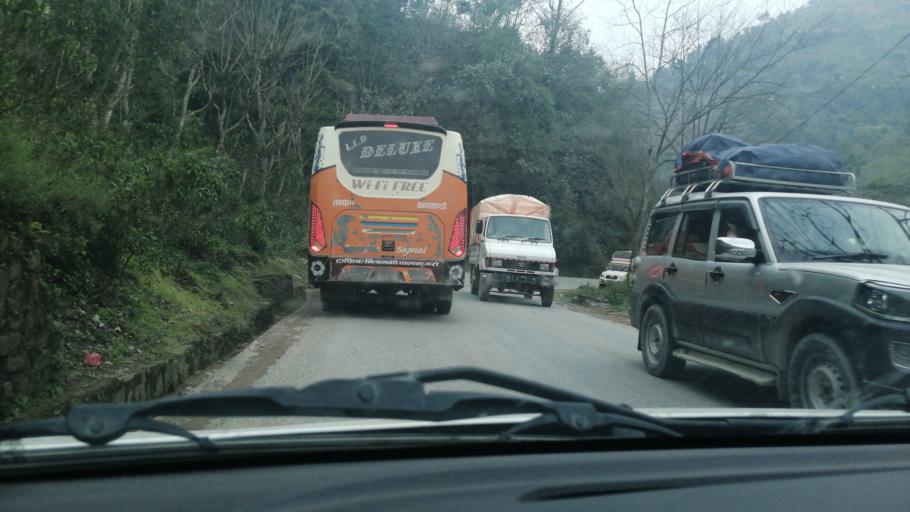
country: NP
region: Western Region
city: Tansen
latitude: 27.8091
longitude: 83.5187
